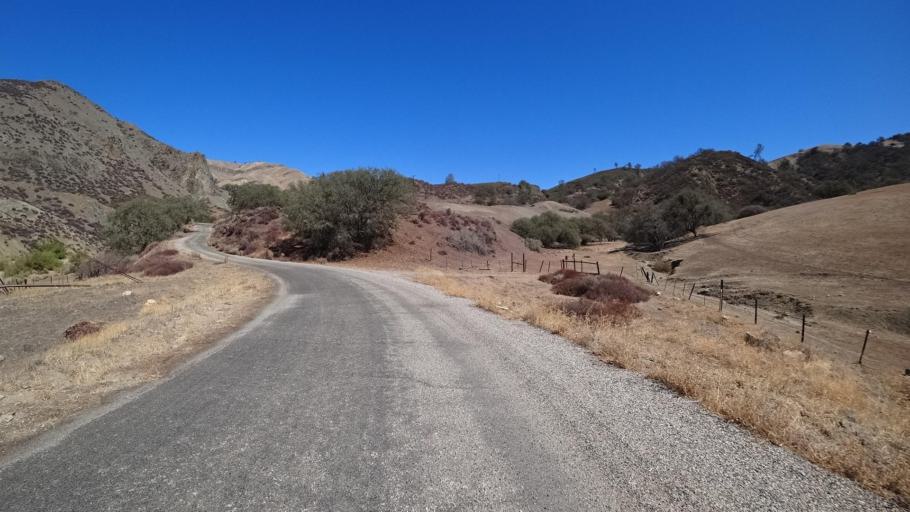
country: US
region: California
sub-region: Monterey County
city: King City
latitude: 36.2916
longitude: -120.8869
